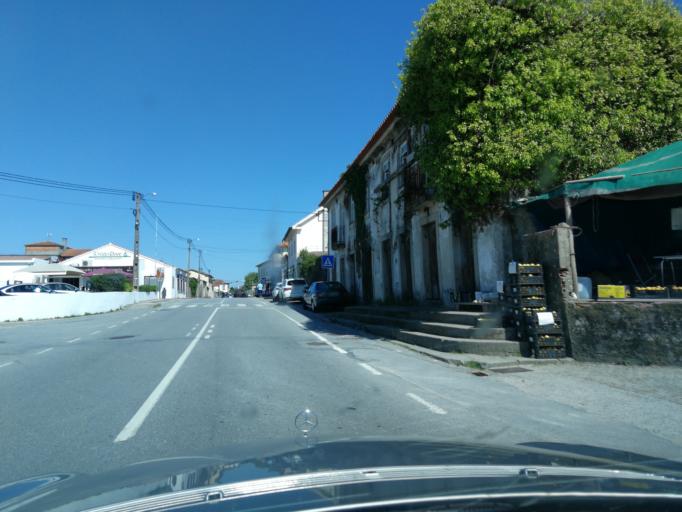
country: PT
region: Viana do Castelo
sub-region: Viana do Castelo
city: Meadela
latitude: 41.7095
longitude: -8.7708
